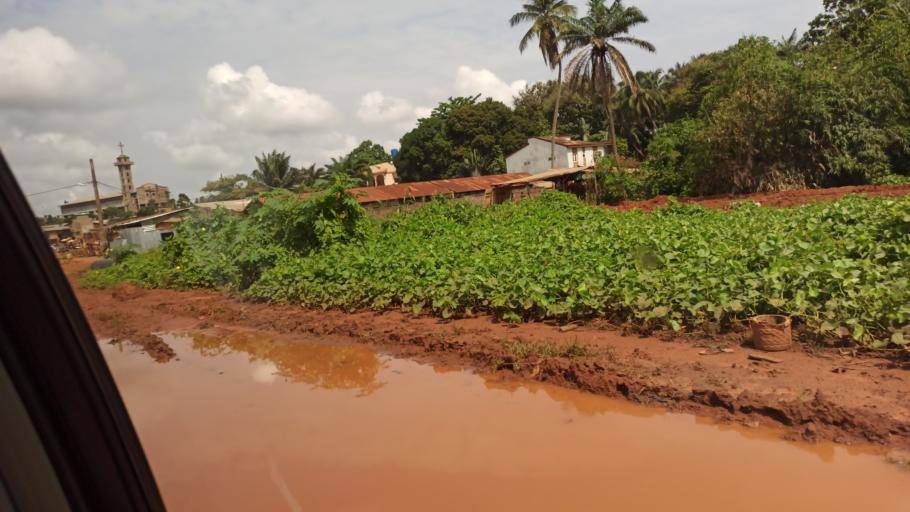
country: BJ
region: Queme
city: Porto-Novo
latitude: 6.4766
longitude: 2.5948
